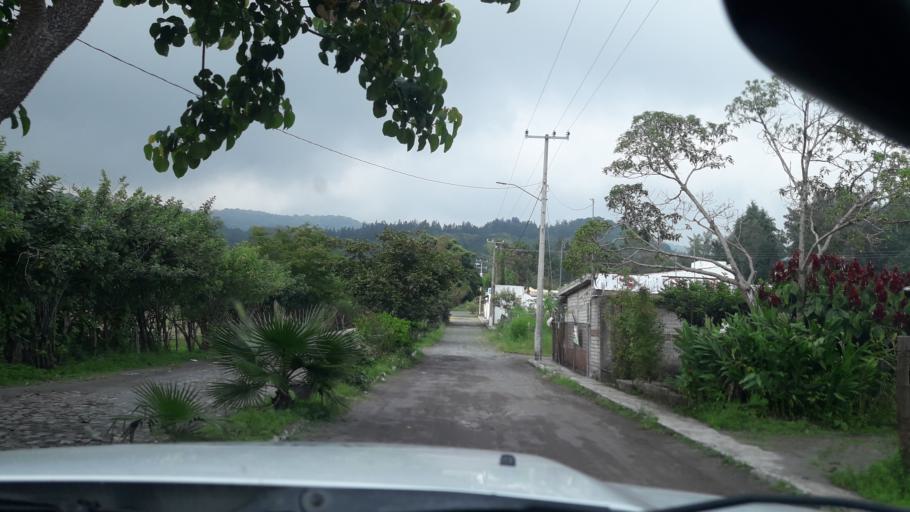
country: MX
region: Colima
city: Suchitlan
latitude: 19.4105
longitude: -103.6553
